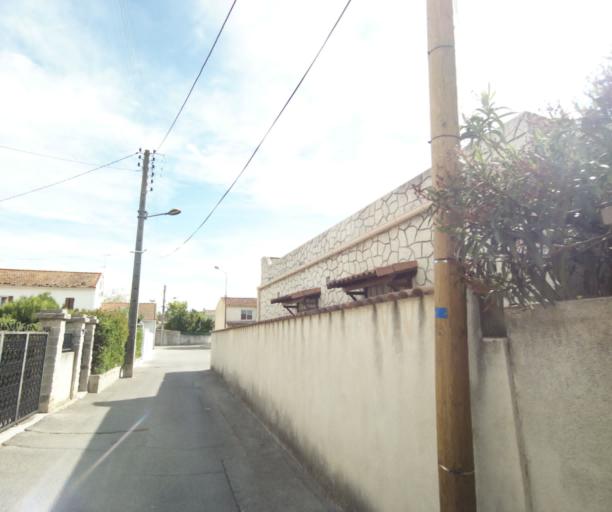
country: FR
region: Provence-Alpes-Cote d'Azur
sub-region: Departement des Bouches-du-Rhone
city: Rognac
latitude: 43.4890
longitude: 5.2269
